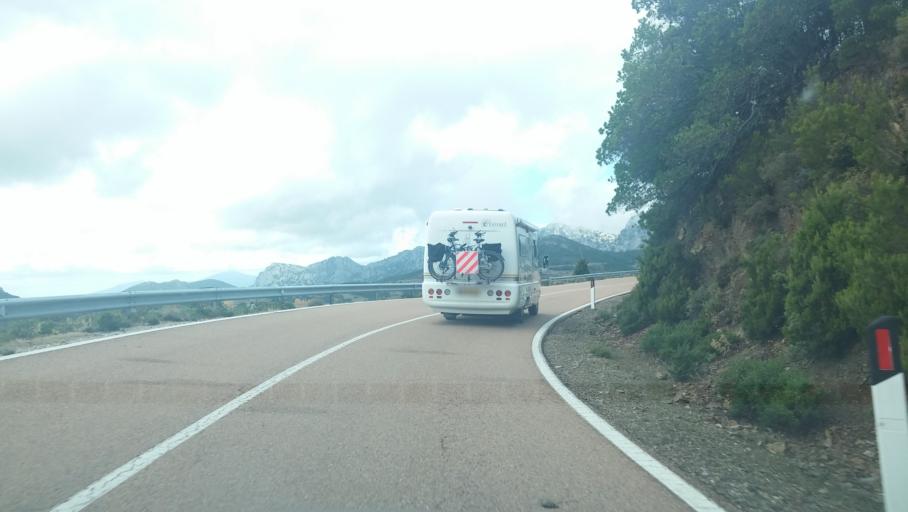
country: IT
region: Sardinia
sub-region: Provincia di Ogliastra
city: Urzulei
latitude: 40.1627
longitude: 9.5249
